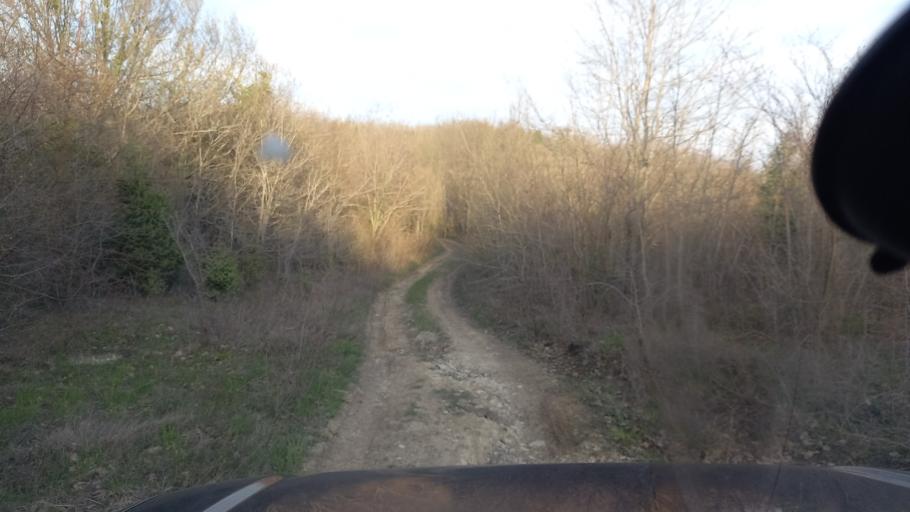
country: RU
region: Krasnodarskiy
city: Arkhipo-Osipovka
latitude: 44.3602
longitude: 38.5546
